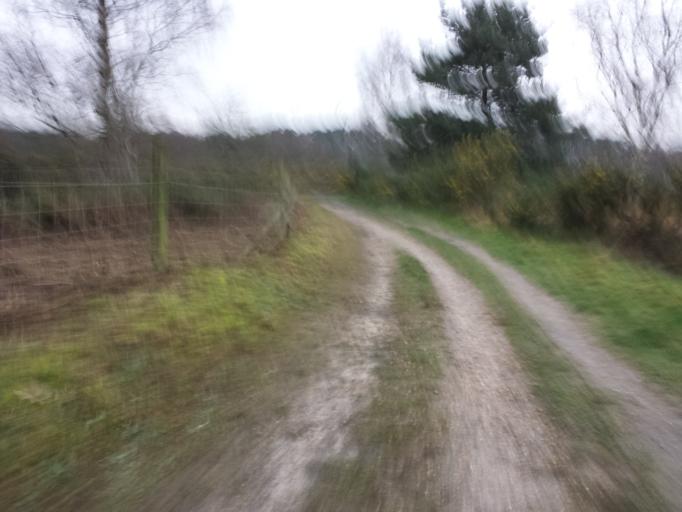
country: GB
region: England
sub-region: Surrey
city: Bagshot
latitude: 51.3508
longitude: -0.6873
